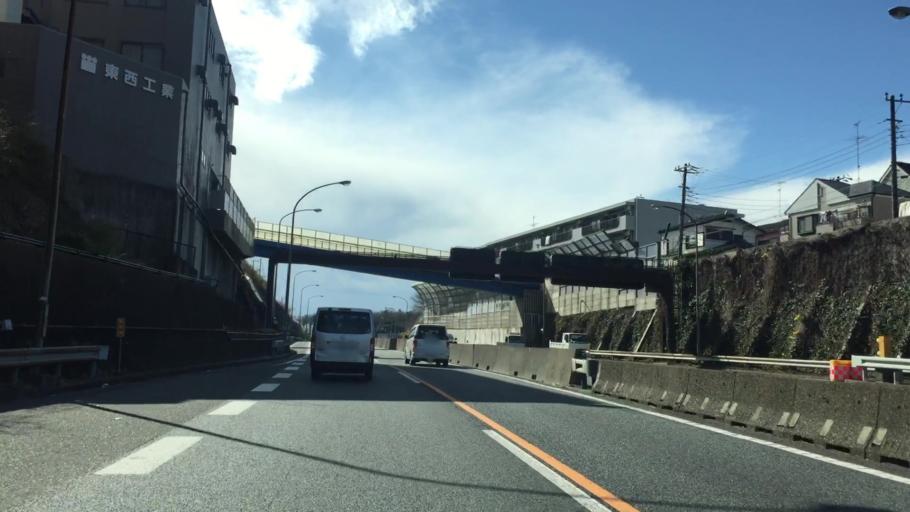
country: JP
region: Kanagawa
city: Yokohama
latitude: 35.4487
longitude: 139.5676
